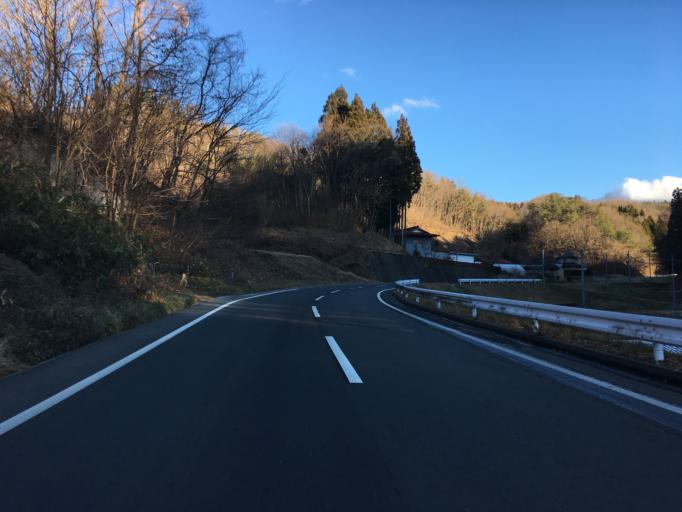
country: JP
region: Fukushima
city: Ishikawa
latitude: 37.2054
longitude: 140.5258
